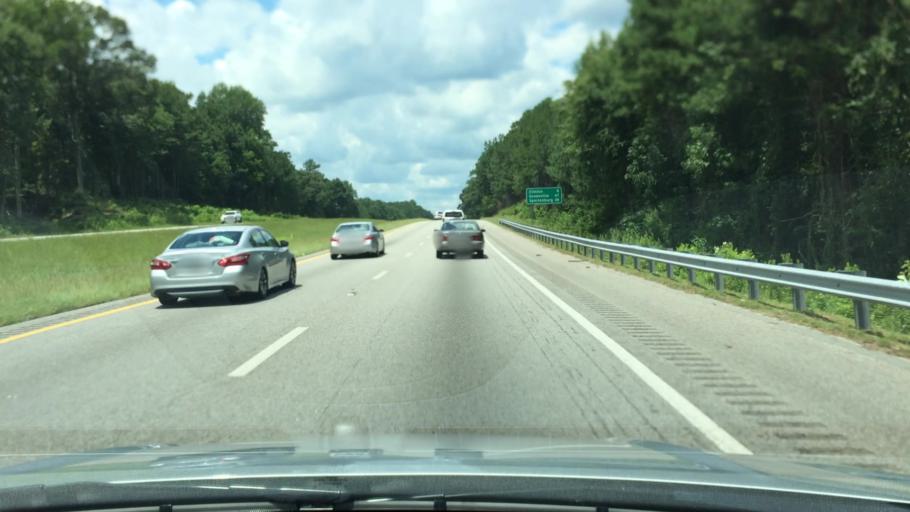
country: US
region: South Carolina
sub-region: Laurens County
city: Joanna
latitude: 34.4467
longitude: -81.7735
